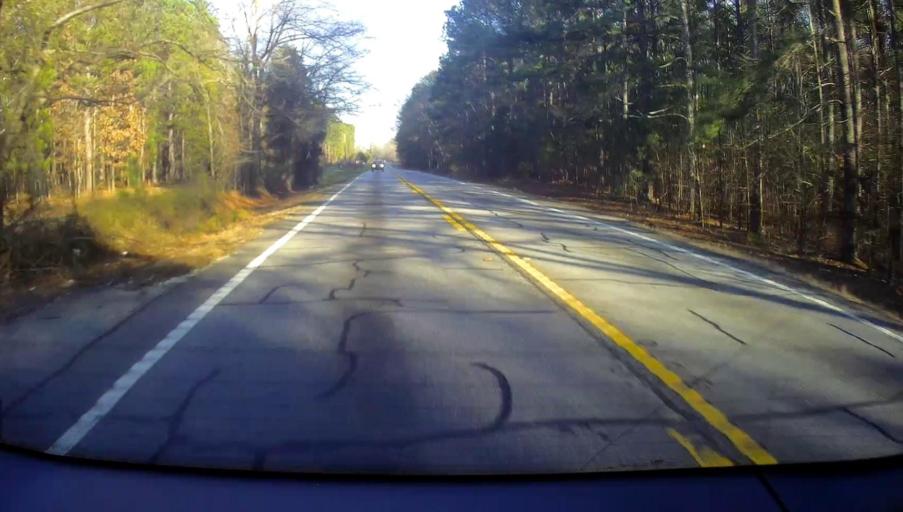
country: US
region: Georgia
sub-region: Henry County
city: Hampton
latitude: 33.4191
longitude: -84.2547
